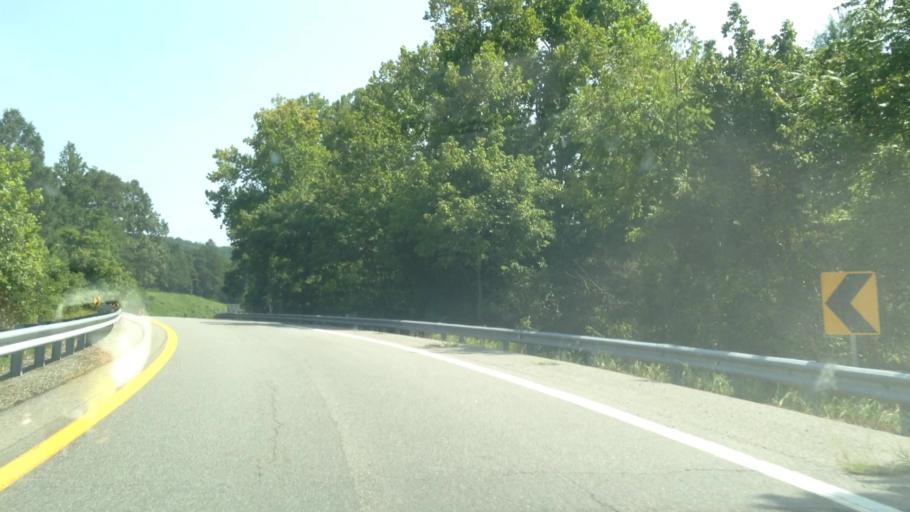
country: US
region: Virginia
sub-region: Henry County
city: Stanleytown
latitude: 36.7370
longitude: -79.9386
